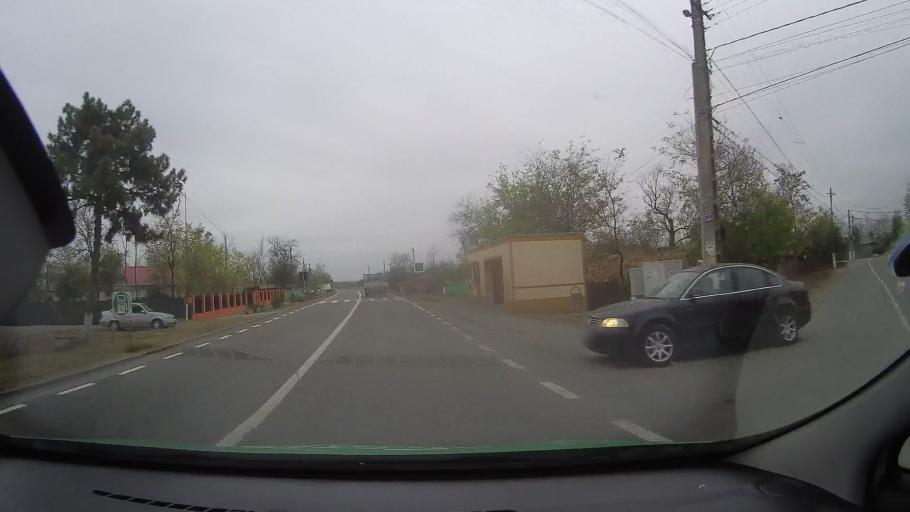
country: RO
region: Ialomita
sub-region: Comuna Scanteia
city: Iazu
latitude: 44.7283
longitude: 27.4251
